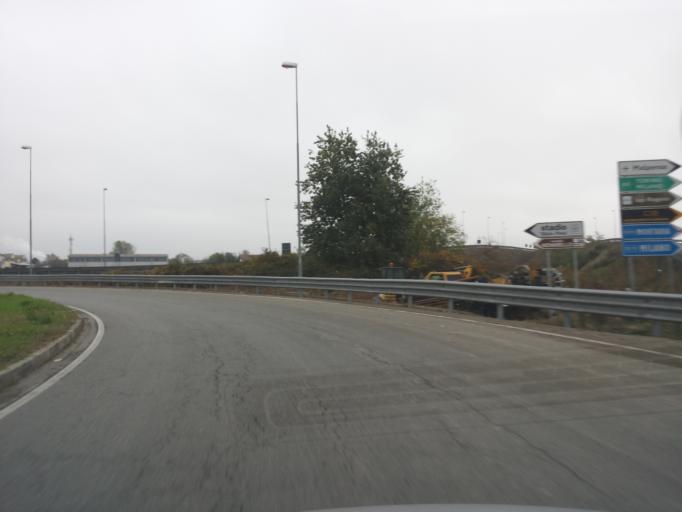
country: IT
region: Piedmont
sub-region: Provincia di Novara
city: Lumellogno
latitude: 45.4190
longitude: 8.5714
